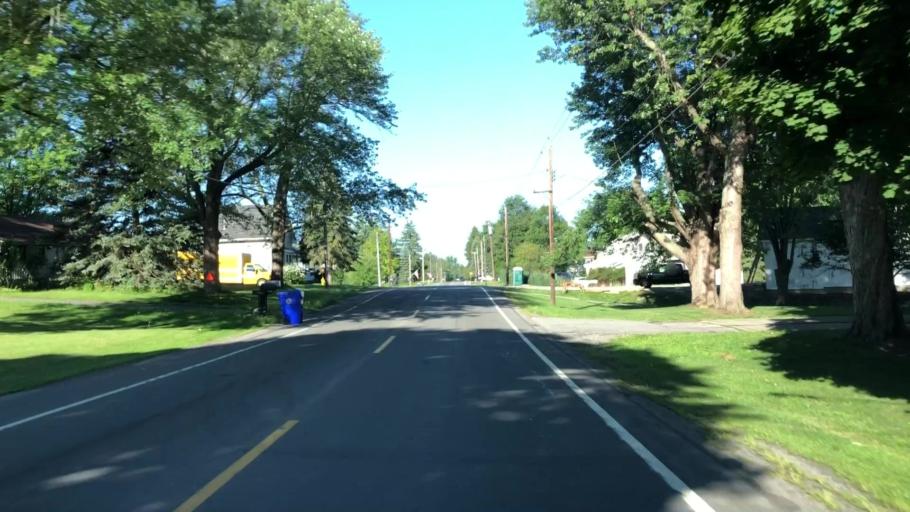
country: US
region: New York
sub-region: Erie County
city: Depew
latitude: 42.8526
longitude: -78.7039
